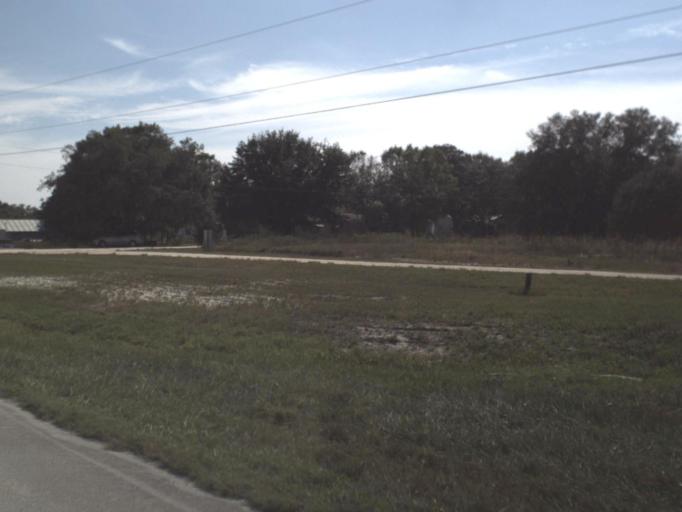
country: US
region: Florida
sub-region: Highlands County
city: Avon Park
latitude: 27.5969
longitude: -81.5398
